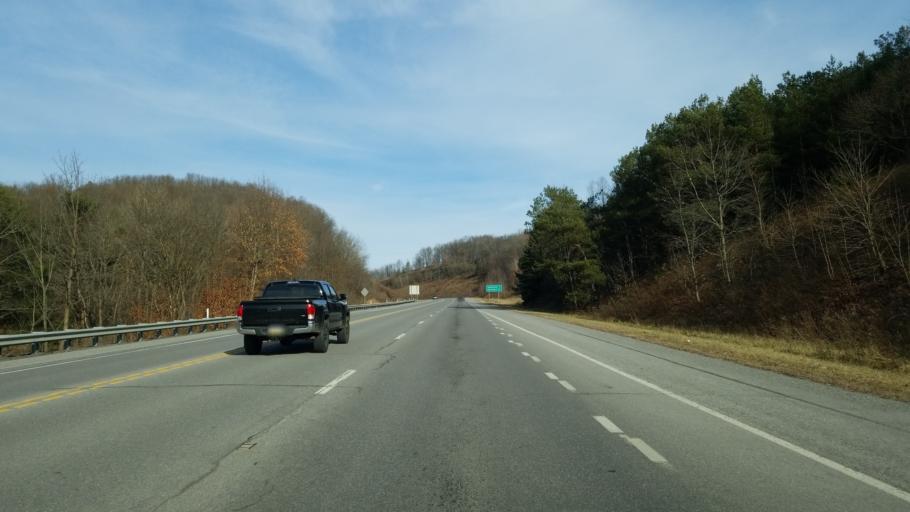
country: US
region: Pennsylvania
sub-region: Clearfield County
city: Clearfield
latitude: 41.0107
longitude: -78.4318
